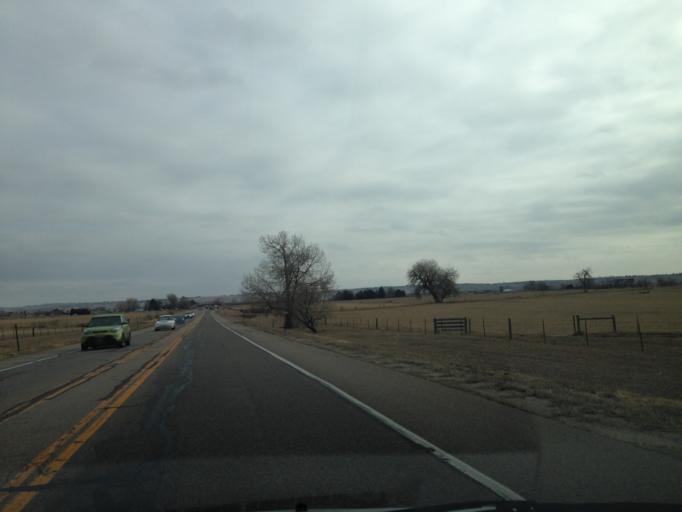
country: US
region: Colorado
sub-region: Boulder County
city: Louisville
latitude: 39.9579
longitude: -105.1373
